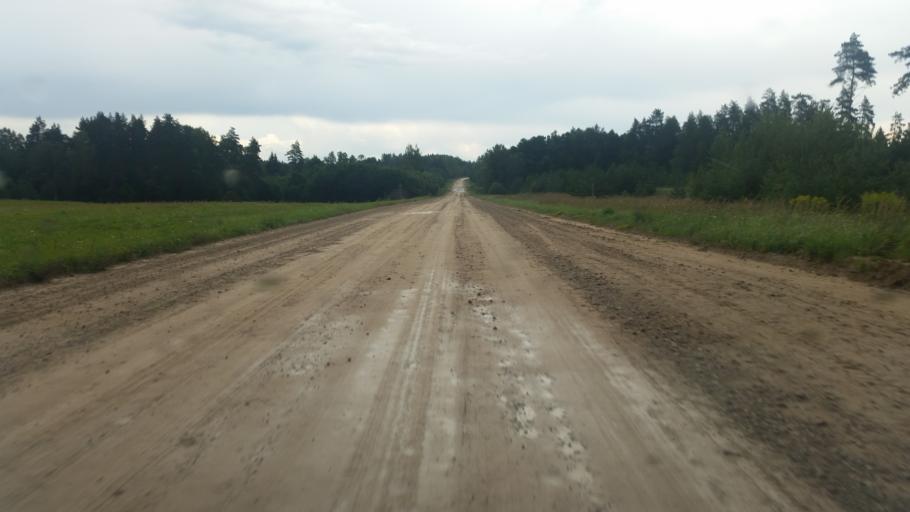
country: LV
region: Vecumnieki
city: Vecumnieki
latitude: 56.4408
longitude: 24.5705
